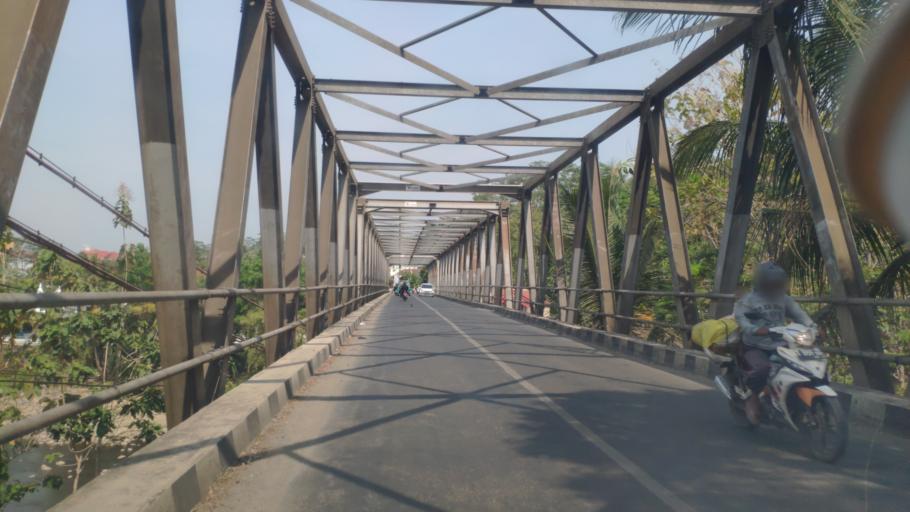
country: ID
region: Central Java
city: Wonosobo
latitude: -7.3890
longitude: 109.6936
